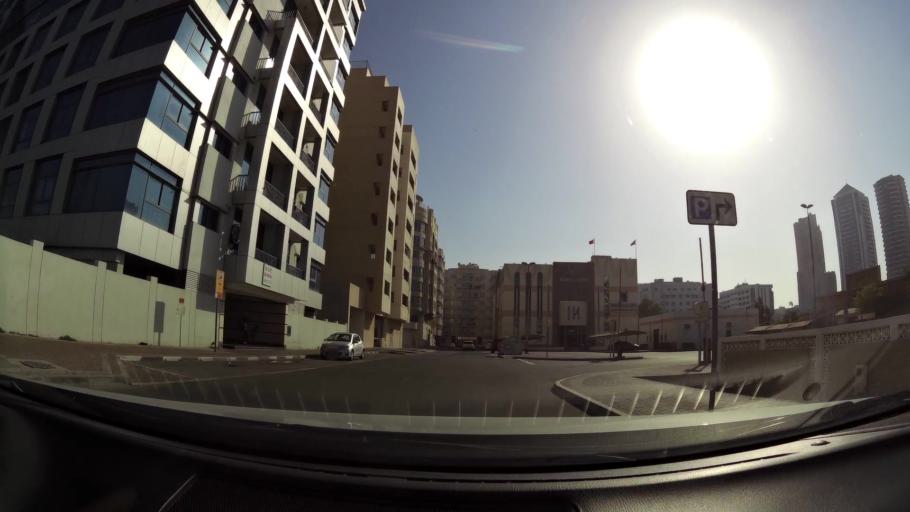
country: AE
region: Ash Shariqah
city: Sharjah
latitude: 25.2543
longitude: 55.2899
